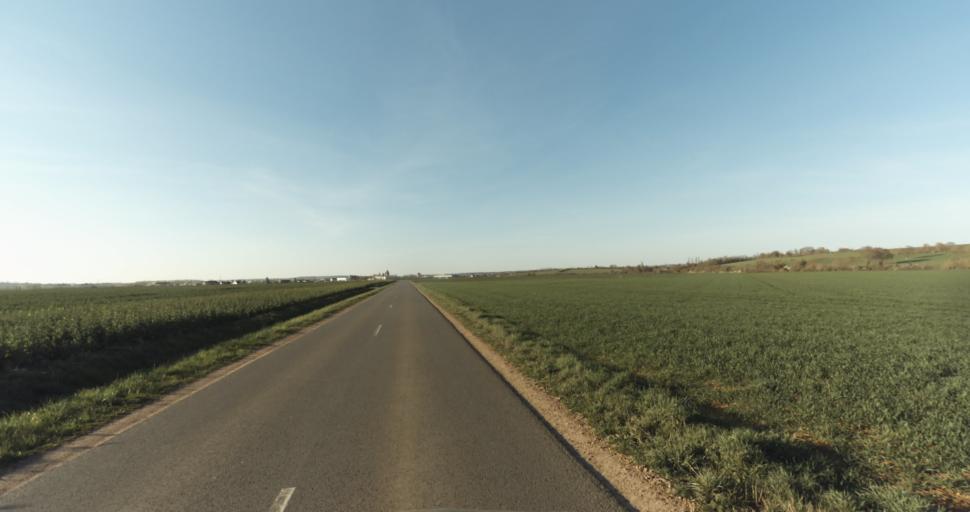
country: FR
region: Lower Normandy
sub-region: Departement du Calvados
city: Saint-Pierre-sur-Dives
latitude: 49.0046
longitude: -0.0245
